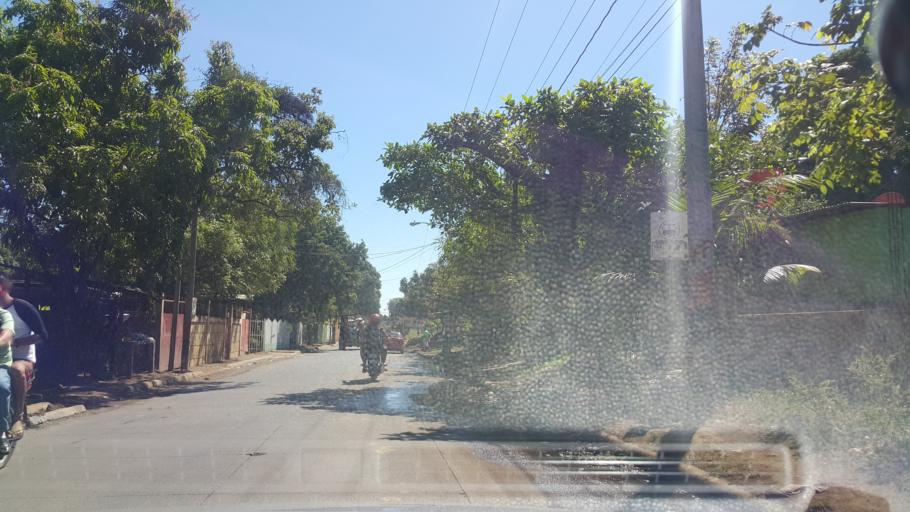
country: NI
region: Managua
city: Managua
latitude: 12.0917
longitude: -86.1996
